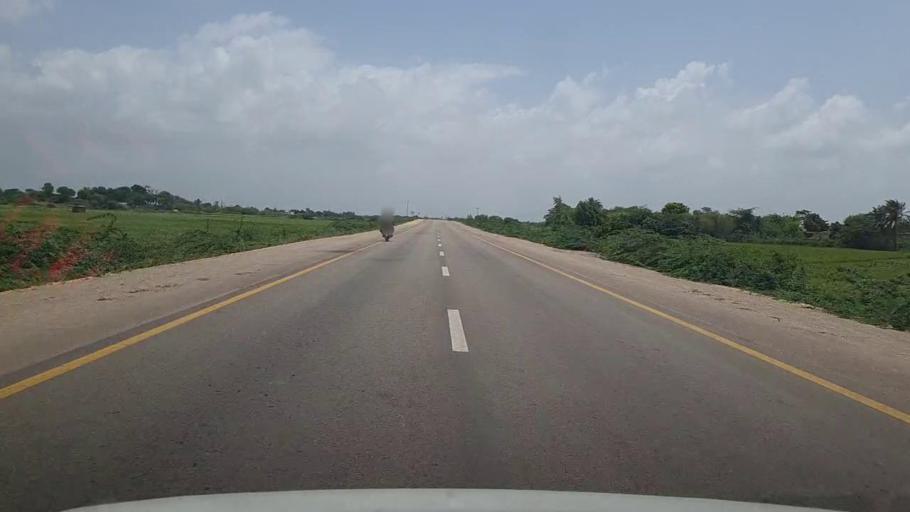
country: PK
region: Sindh
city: Thatta
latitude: 24.7649
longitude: 67.9470
